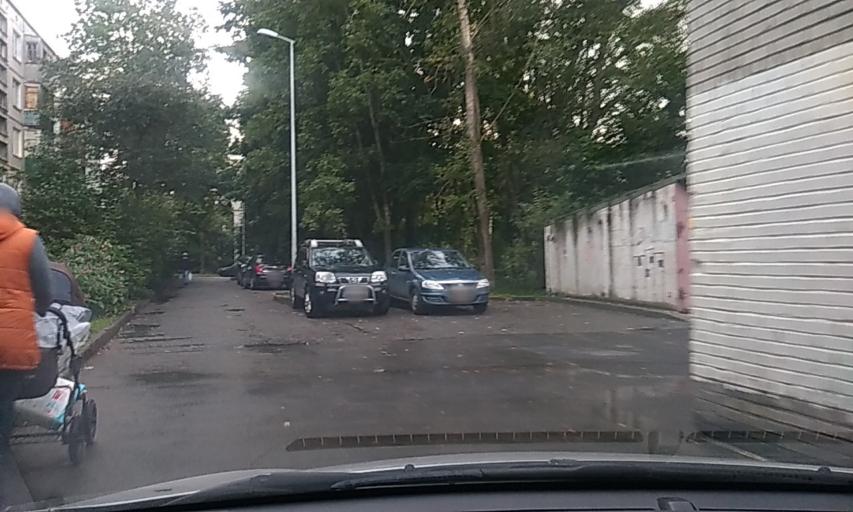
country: RU
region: St.-Petersburg
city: Dachnoye
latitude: 59.8380
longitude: 30.2187
